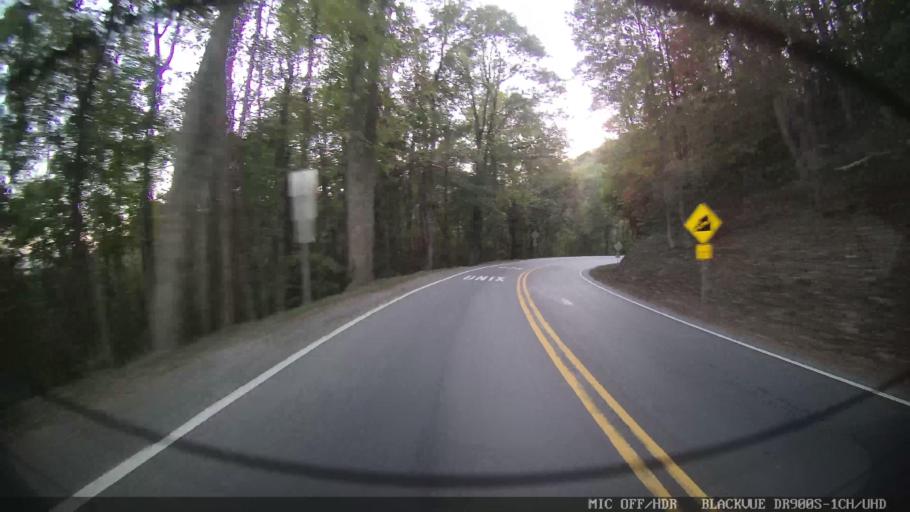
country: US
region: Georgia
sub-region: Union County
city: Blairsville
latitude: 34.7344
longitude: -83.9186
